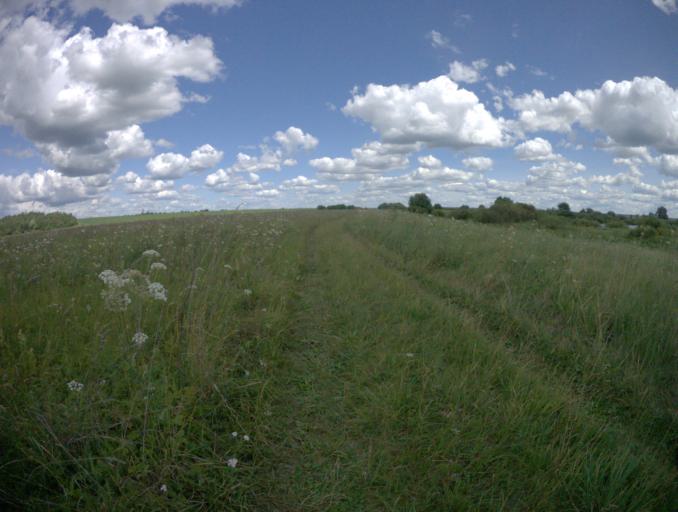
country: RU
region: Vladimir
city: Orgtrud
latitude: 56.3056
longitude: 40.6313
